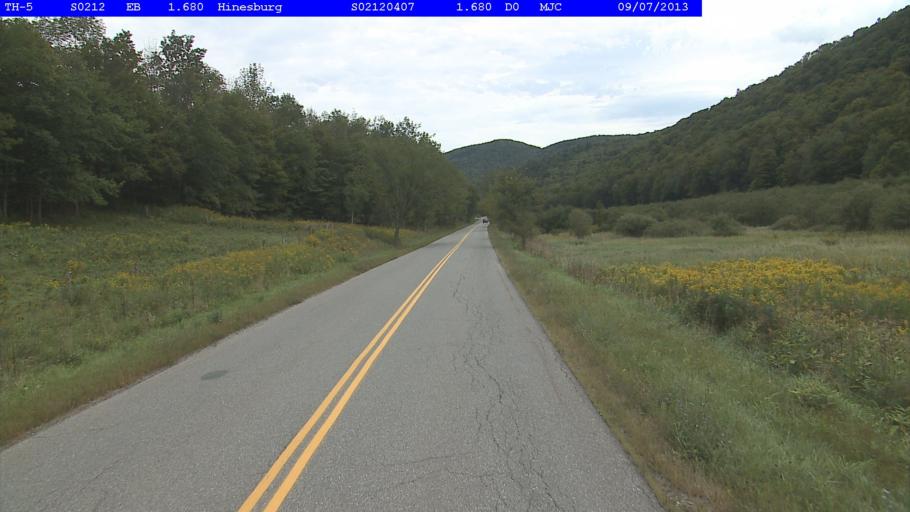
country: US
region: Vermont
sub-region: Chittenden County
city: Hinesburg
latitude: 44.2910
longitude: -73.0377
